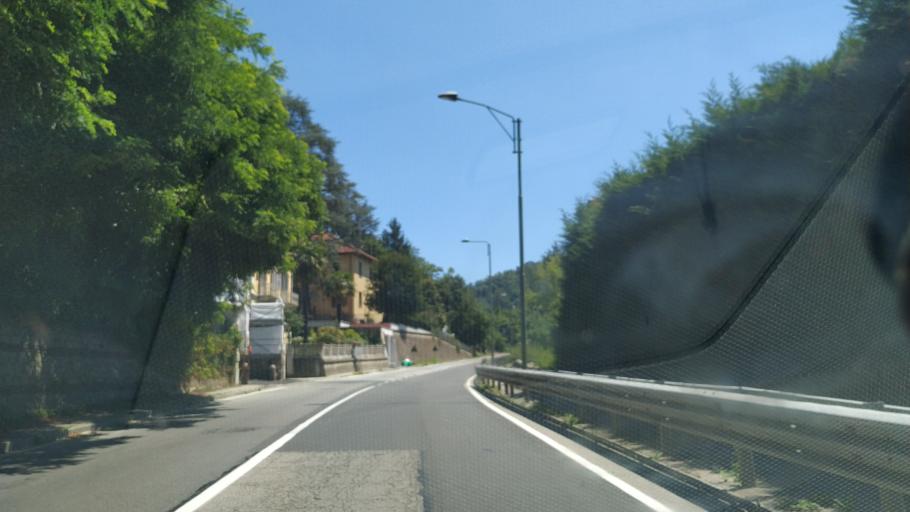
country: IT
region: Piedmont
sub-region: Provincia di Torino
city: San Mauro Torinese
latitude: 45.0792
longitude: 7.7377
